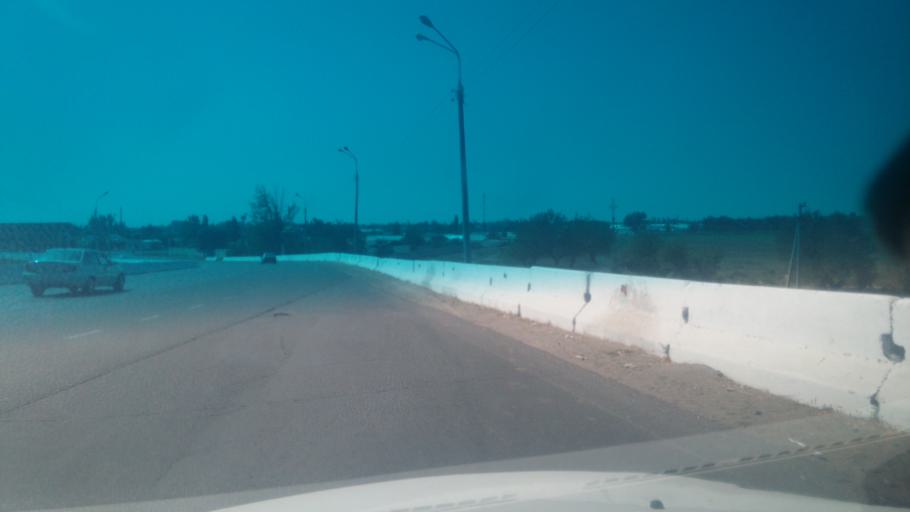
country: UZ
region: Sirdaryo
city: Sirdaryo
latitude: 40.8029
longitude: 68.6763
